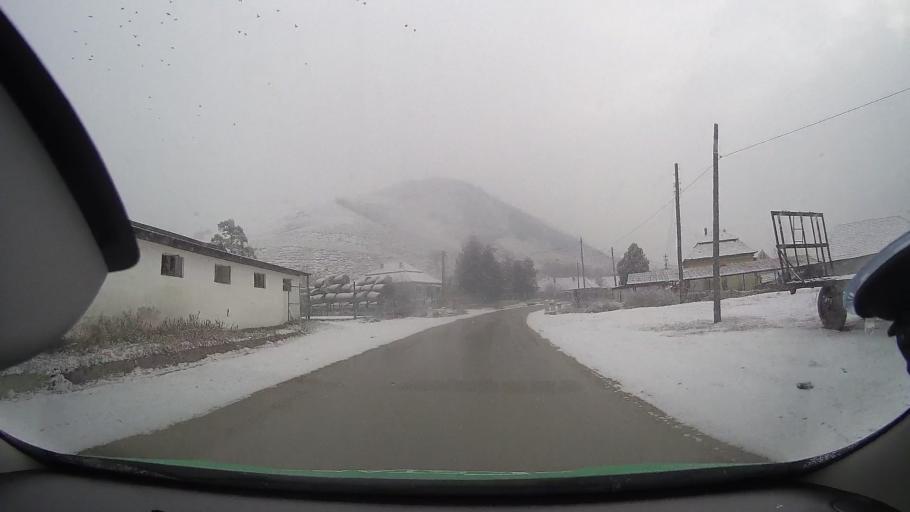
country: RO
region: Alba
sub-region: Comuna Lopadea Noua
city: Lopadea Noua
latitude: 46.2983
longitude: 23.8127
